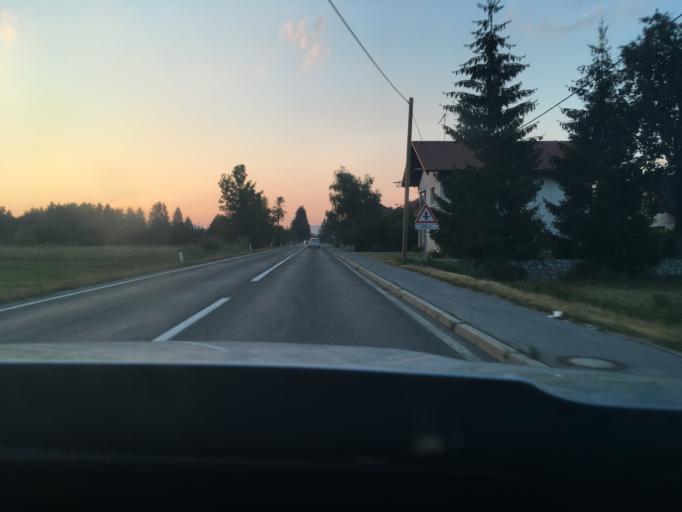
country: SI
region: Ribnica
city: Ribnica
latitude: 45.7236
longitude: 14.7412
